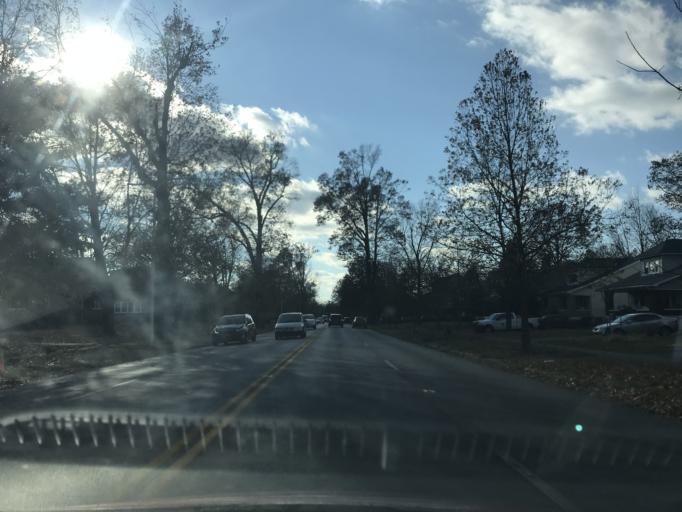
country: US
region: Kentucky
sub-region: Jefferson County
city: Audubon Park
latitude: 38.2168
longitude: -85.7391
